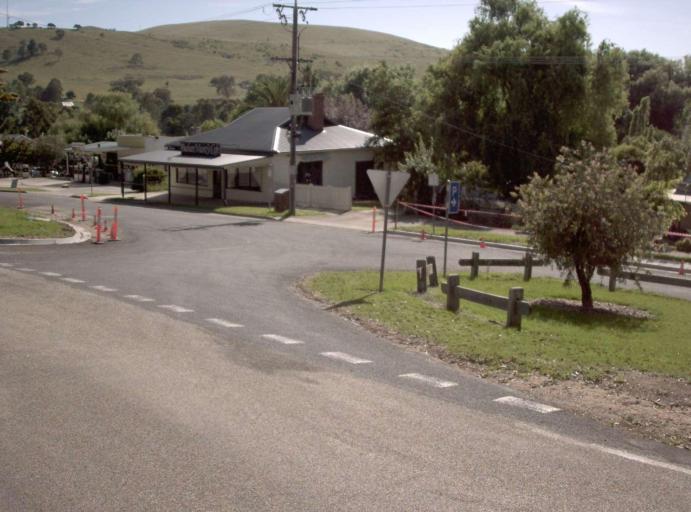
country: AU
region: Victoria
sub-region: East Gippsland
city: Lakes Entrance
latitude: -37.4998
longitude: 148.1718
